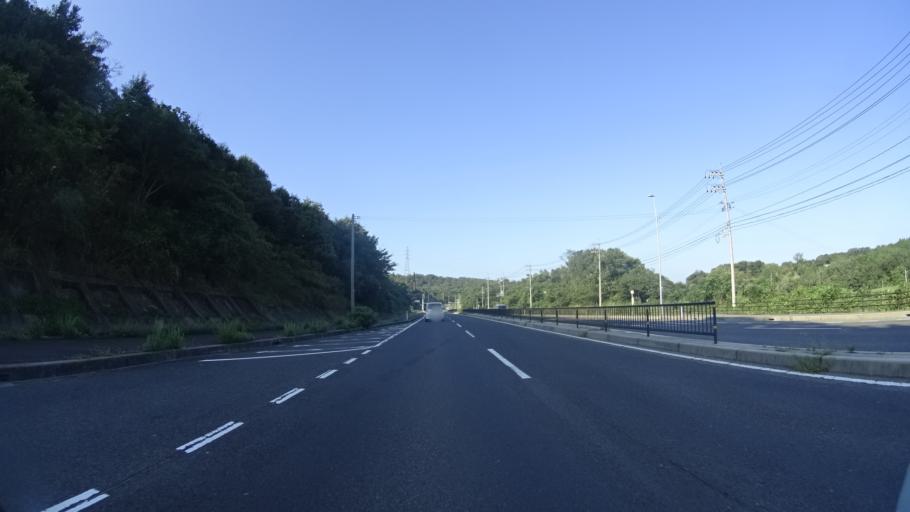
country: JP
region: Shimane
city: Matsue-shi
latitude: 35.5099
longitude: 133.1134
